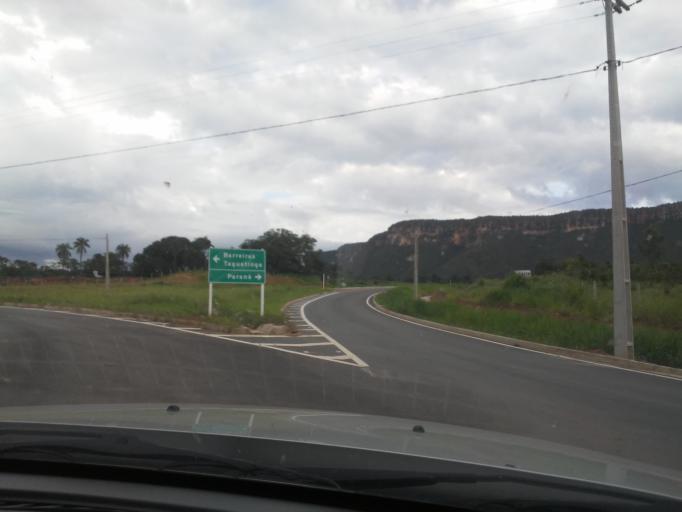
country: BR
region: Tocantins
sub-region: Taguatinga
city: Taguatinga
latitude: -12.3882
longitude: -46.4130
